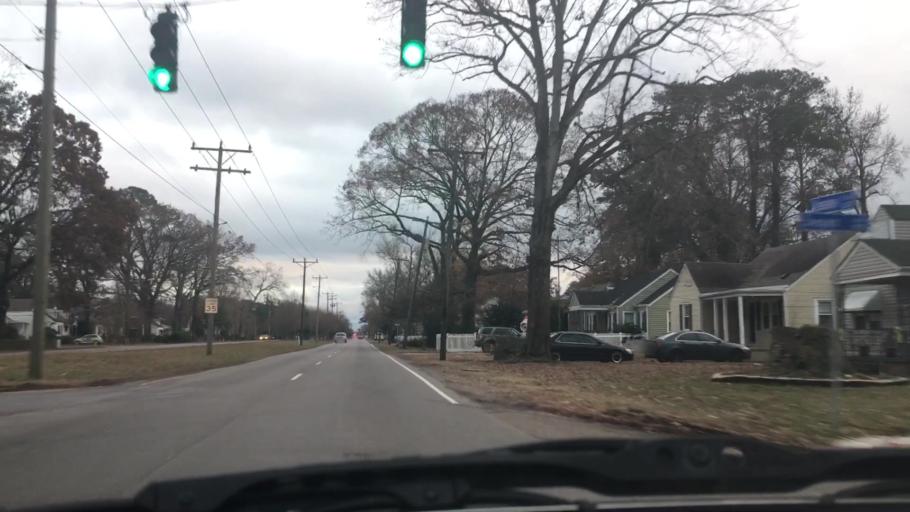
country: US
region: Virginia
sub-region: City of Norfolk
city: Norfolk
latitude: 36.9238
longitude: -76.2430
